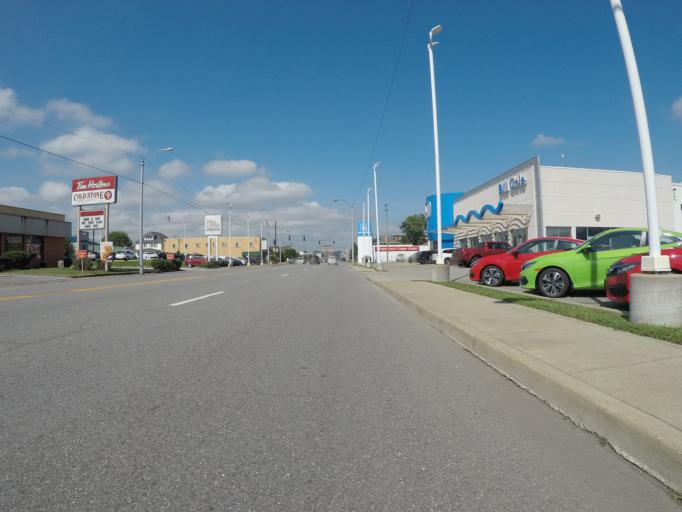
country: US
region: Kentucky
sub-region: Boyd County
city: Ashland
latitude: 38.4726
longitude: -82.6274
